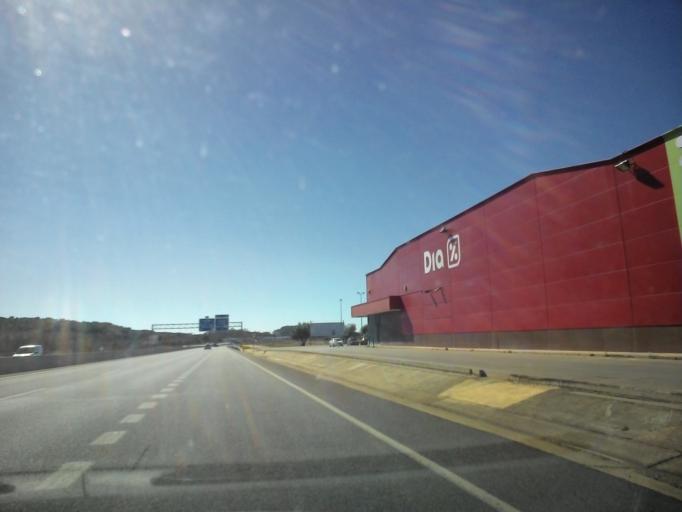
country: ES
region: Catalonia
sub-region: Provincia de Girona
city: Palamos
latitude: 41.8714
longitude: 3.1382
